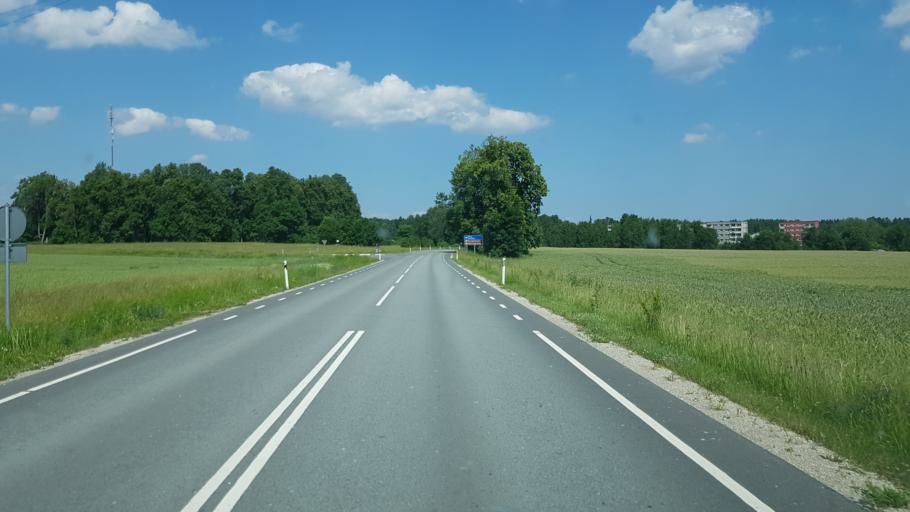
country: EE
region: Tartu
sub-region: Alatskivi vald
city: Kallaste
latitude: 58.5945
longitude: 27.1265
